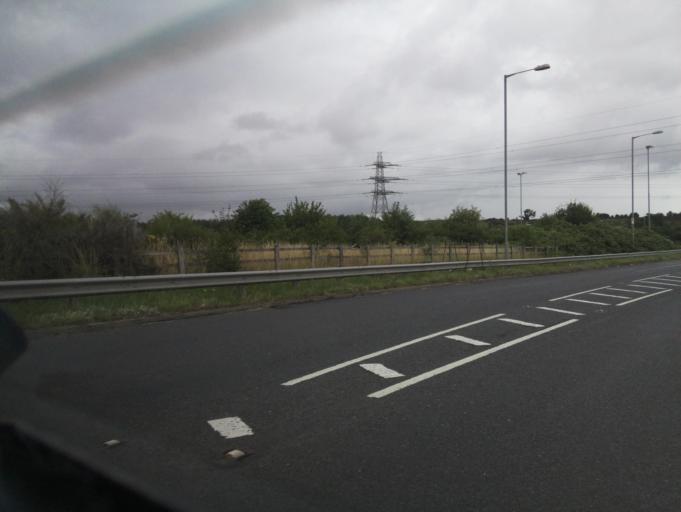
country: GB
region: England
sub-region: Worcestershire
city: Fernhill Heath
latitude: 52.2175
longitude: -2.1607
